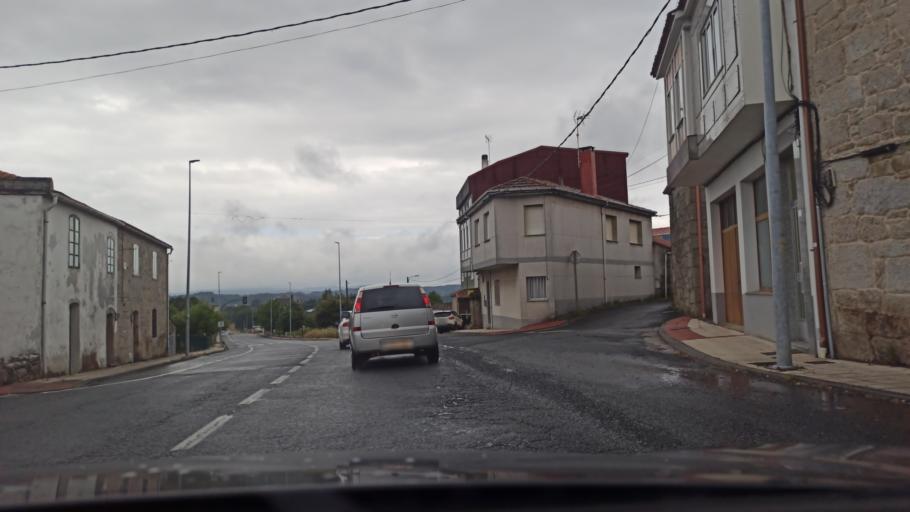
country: ES
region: Galicia
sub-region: Provincia de Lugo
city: Monterroso
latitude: 42.7932
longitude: -7.8393
